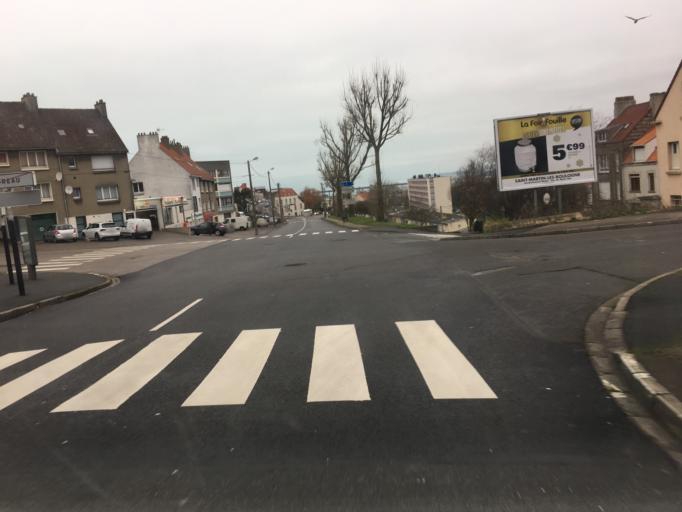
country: FR
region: Nord-Pas-de-Calais
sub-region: Departement du Pas-de-Calais
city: Outreau
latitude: 50.7147
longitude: 1.5917
